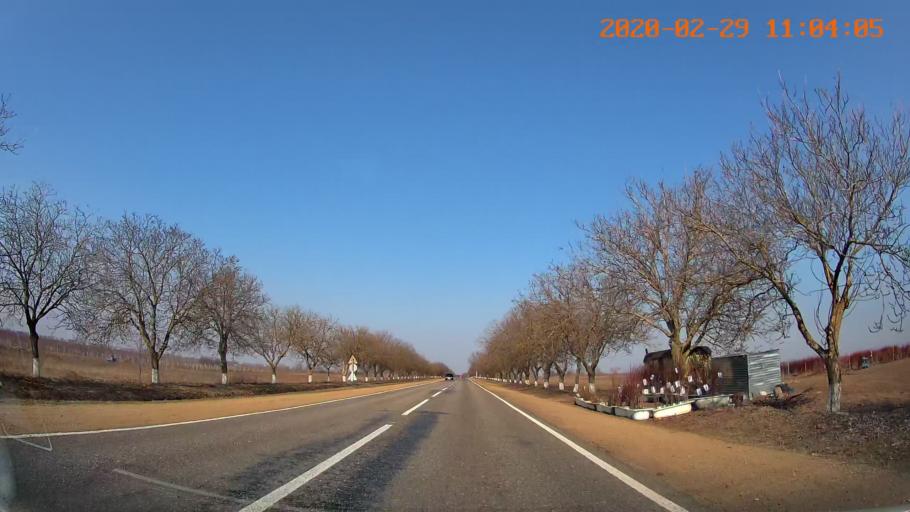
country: MD
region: Criuleni
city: Criuleni
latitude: 47.1846
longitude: 29.2064
